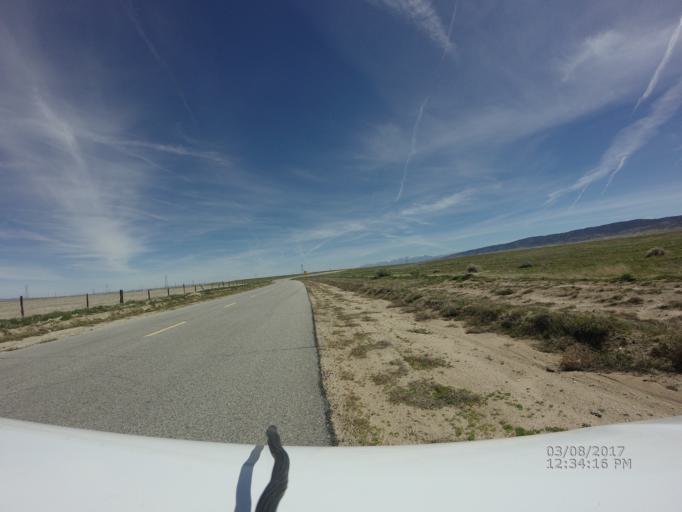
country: US
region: California
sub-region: Los Angeles County
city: Leona Valley
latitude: 34.7114
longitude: -118.3454
